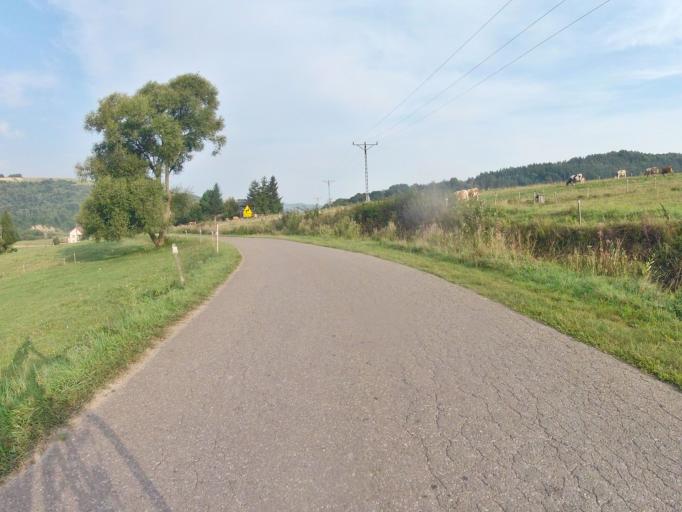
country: PL
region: Subcarpathian Voivodeship
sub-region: Powiat jasielski
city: Krempna
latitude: 49.5463
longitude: 21.5508
